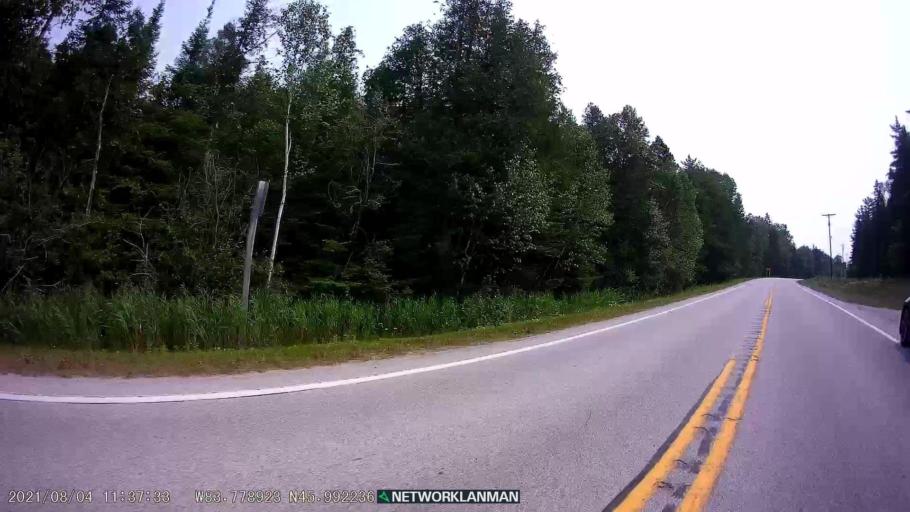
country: CA
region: Ontario
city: Thessalon
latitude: 45.9920
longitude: -83.7789
